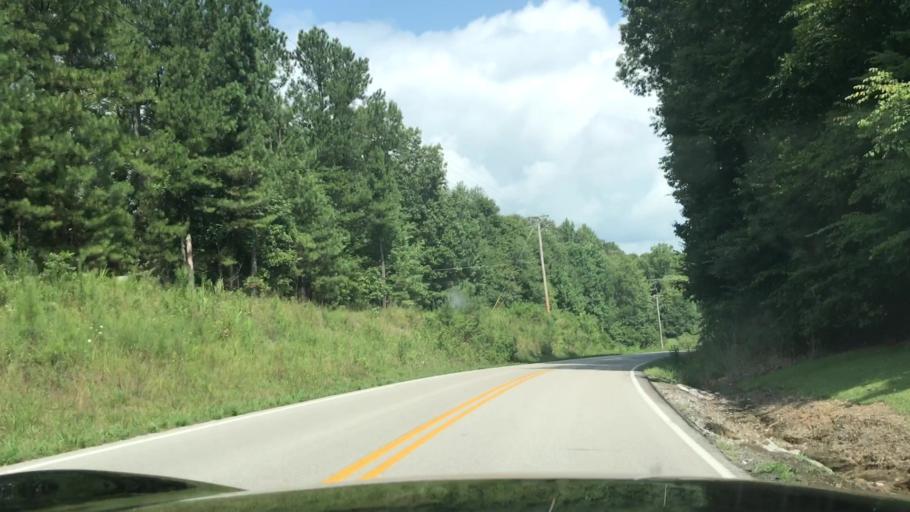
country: US
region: Kentucky
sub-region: Ohio County
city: Oak Grove
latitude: 37.1918
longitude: -86.8828
